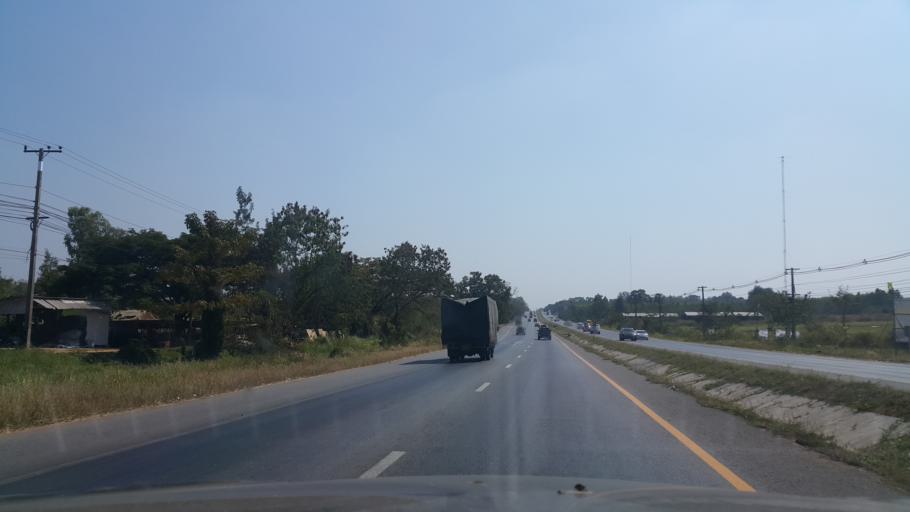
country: TH
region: Khon Kaen
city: Nam Phong
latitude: 16.5785
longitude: 102.8208
